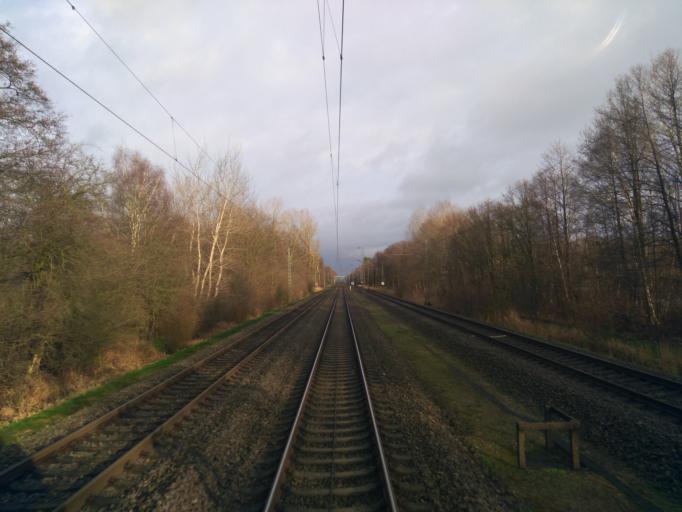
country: DE
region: Lower Saxony
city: Konigsmoor
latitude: 53.2455
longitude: 9.6745
